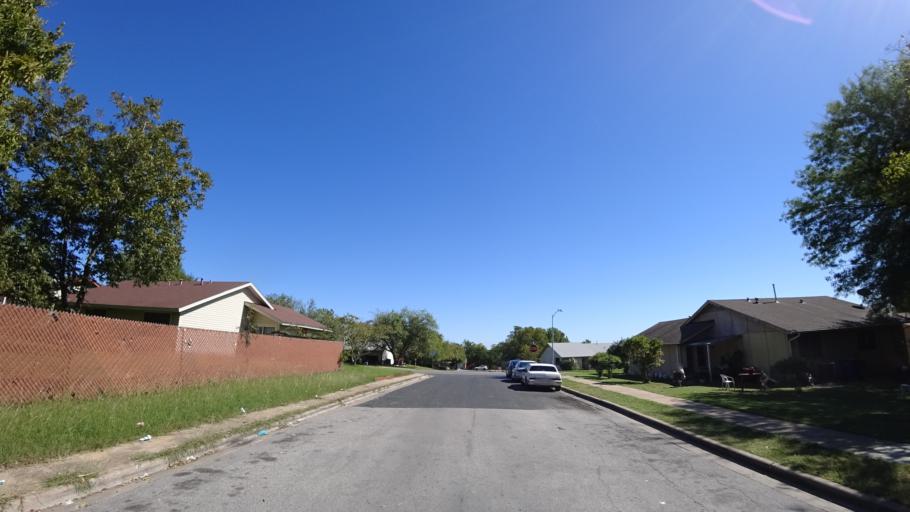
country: US
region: Texas
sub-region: Travis County
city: Hornsby Bend
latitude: 30.3011
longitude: -97.6434
